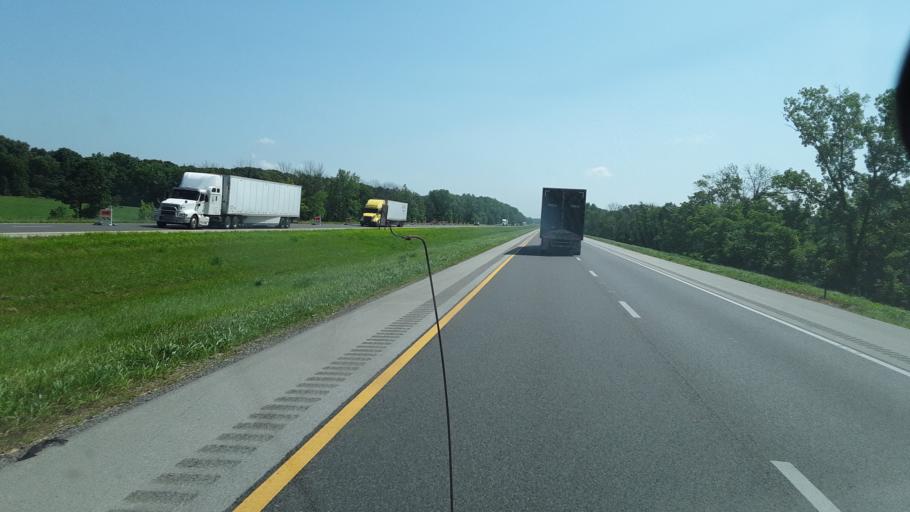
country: US
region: Illinois
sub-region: Cumberland County
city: Toledo
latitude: 39.2036
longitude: -88.2874
